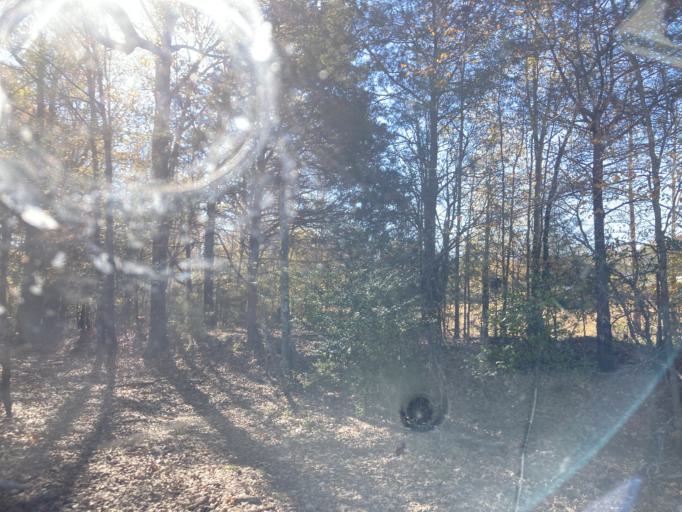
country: US
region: Mississippi
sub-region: Holmes County
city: Pickens
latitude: 32.8567
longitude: -90.0067
